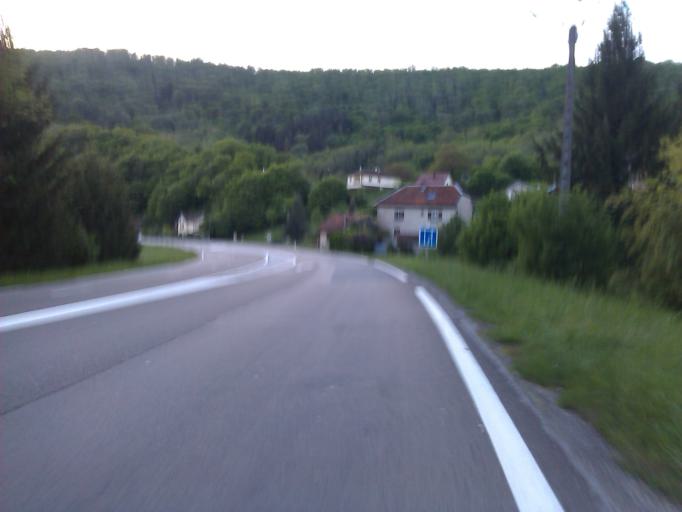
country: FR
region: Franche-Comte
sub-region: Departement du Doubs
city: Baume-les-Dames
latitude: 47.3716
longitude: 6.4289
